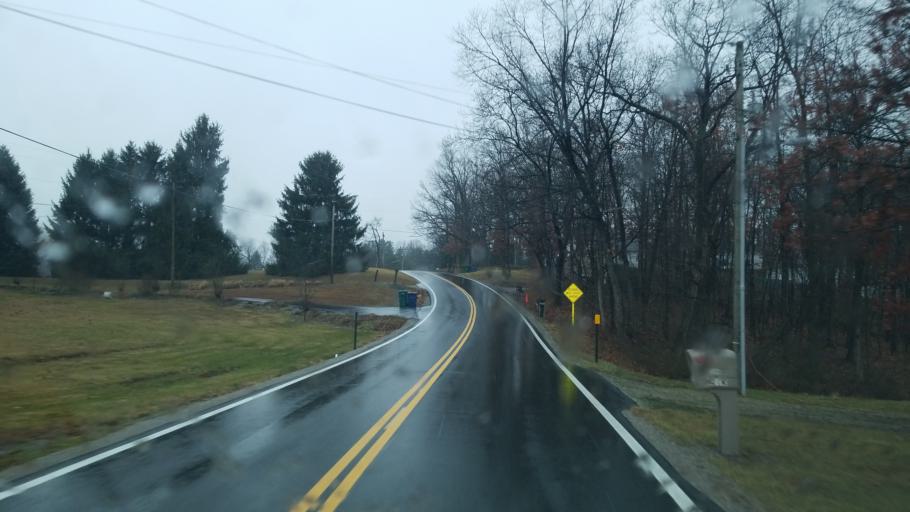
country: US
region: Ohio
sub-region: Licking County
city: Newark
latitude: 40.0919
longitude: -82.3547
